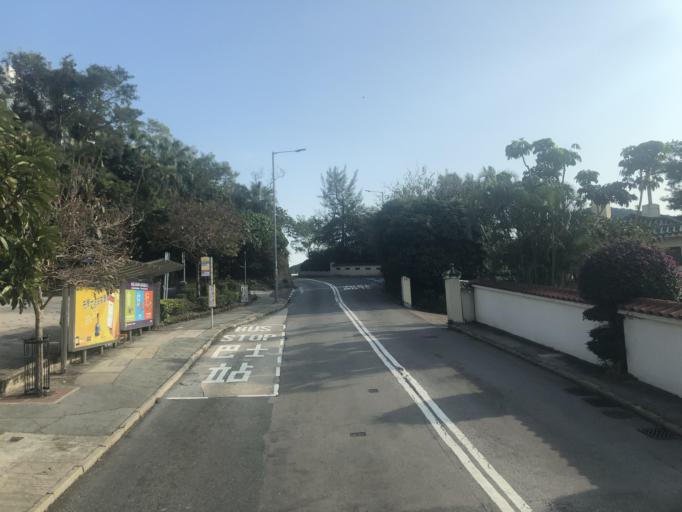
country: HK
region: Wanchai
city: Wan Chai
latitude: 22.2405
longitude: 114.1873
